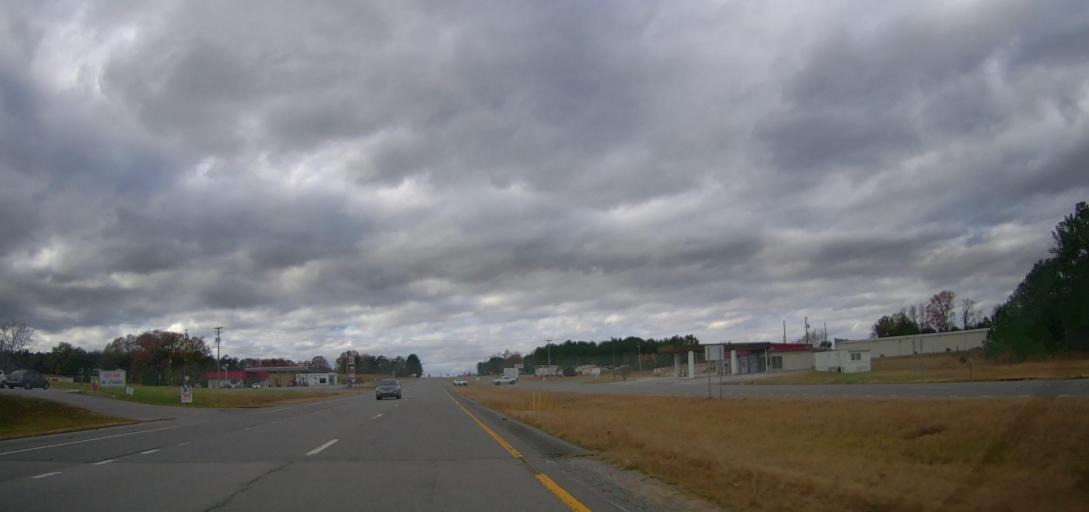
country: US
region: Alabama
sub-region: Lawrence County
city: Town Creek
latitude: 34.5882
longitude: -87.4229
